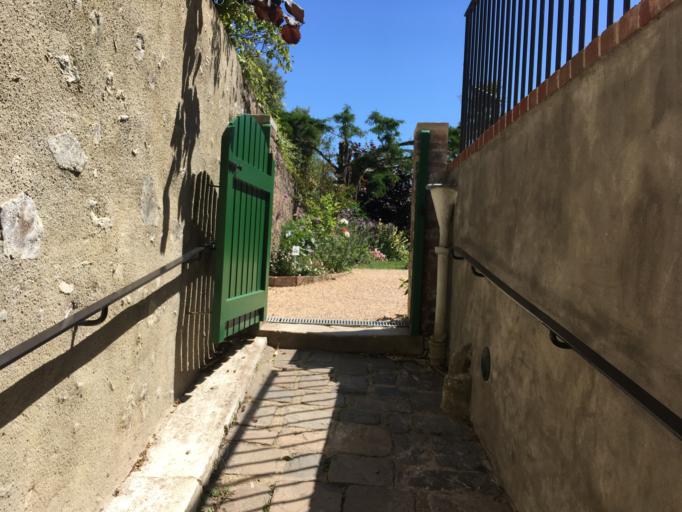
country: GG
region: St Peter Port
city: Saint Peter Port
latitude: 49.4513
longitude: -2.5375
